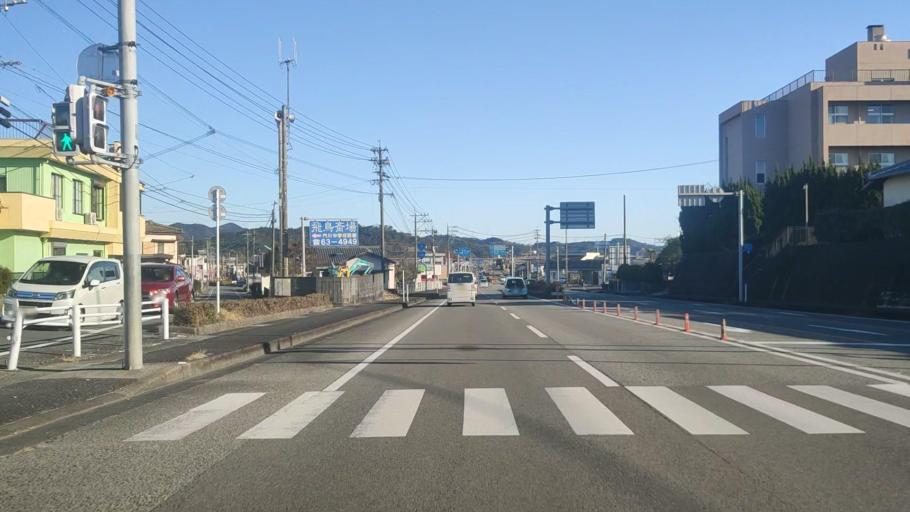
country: JP
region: Miyazaki
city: Nobeoka
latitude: 32.4730
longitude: 131.6519
